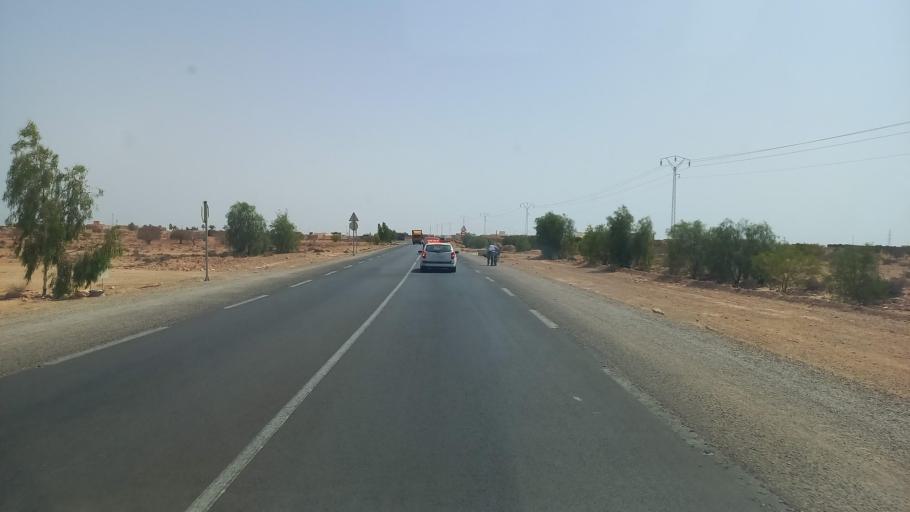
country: TN
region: Madanin
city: Medenine
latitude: 33.3694
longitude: 10.6824
